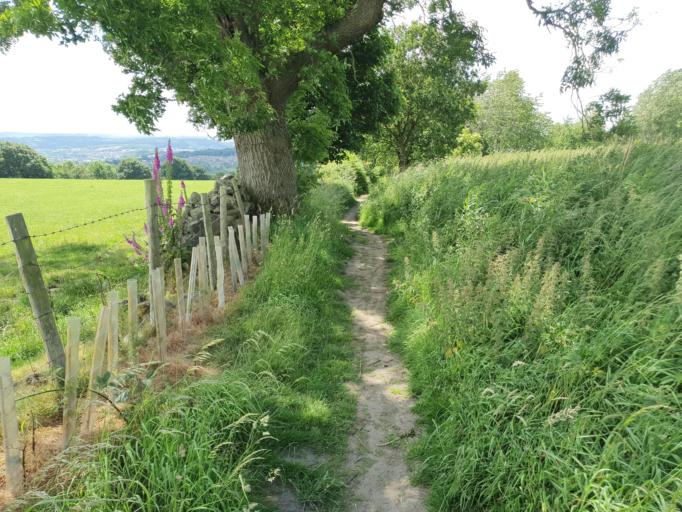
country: GB
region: England
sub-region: City and Borough of Leeds
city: Guiseley
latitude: 53.8655
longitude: -1.7346
